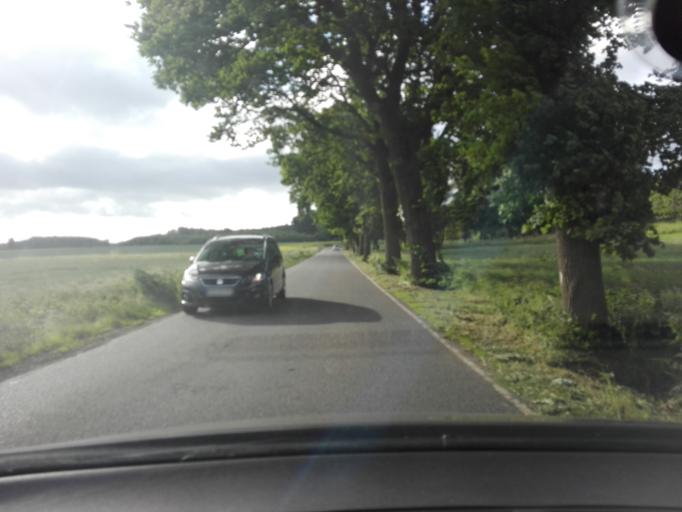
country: DE
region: North Rhine-Westphalia
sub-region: Regierungsbezirk Arnsberg
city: Frondenberg
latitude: 51.4996
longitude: 7.7463
